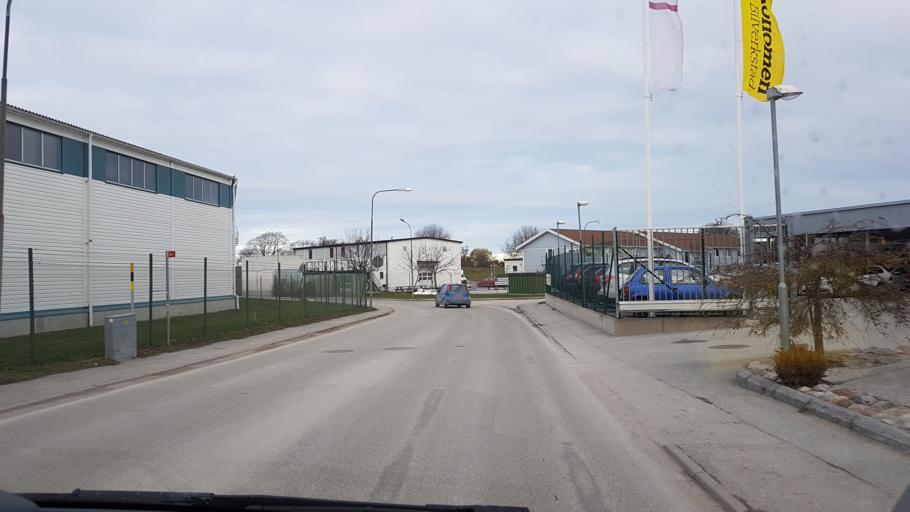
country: SE
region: Gotland
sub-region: Gotland
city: Visby
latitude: 57.6457
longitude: 18.3159
